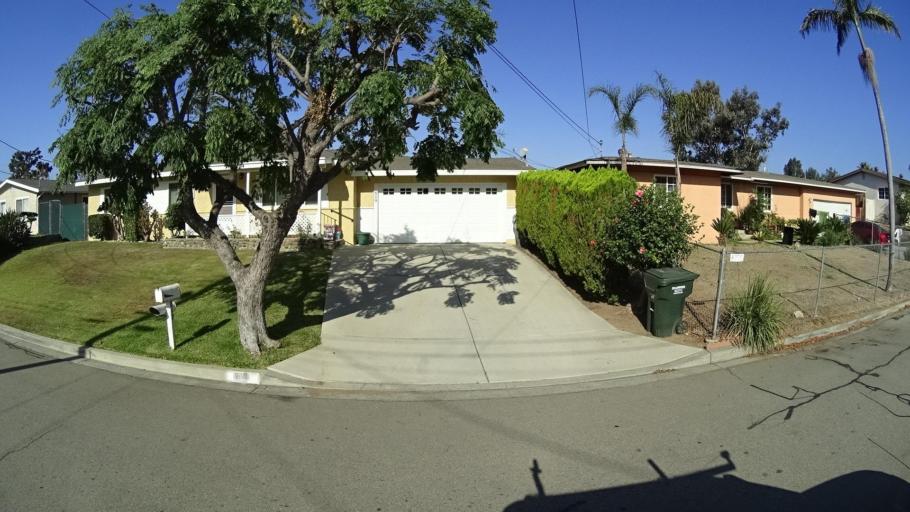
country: US
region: California
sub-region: San Diego County
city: Fallbrook
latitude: 33.3741
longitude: -117.2353
